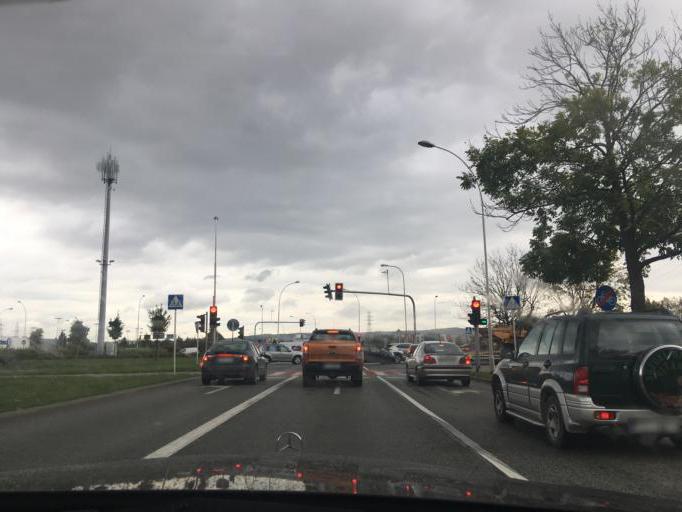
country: PL
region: Subcarpathian Voivodeship
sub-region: Rzeszow
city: Rzeszow
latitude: 50.0177
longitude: 22.0161
